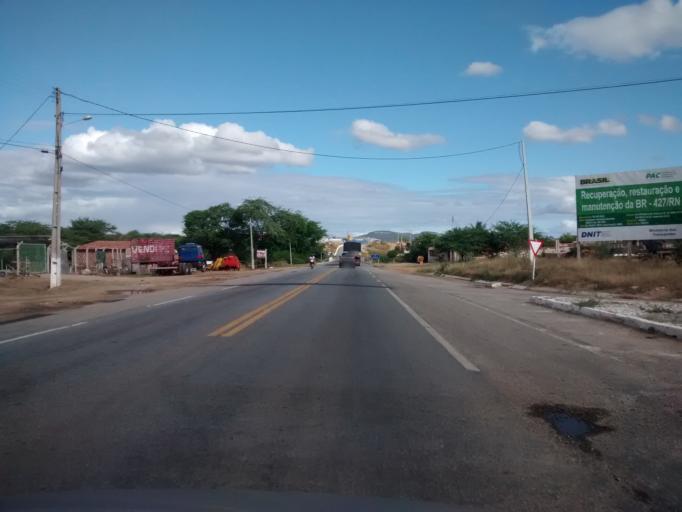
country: BR
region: Rio Grande do Norte
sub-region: Currais Novos
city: Currais Novos
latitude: -6.2775
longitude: -36.5225
